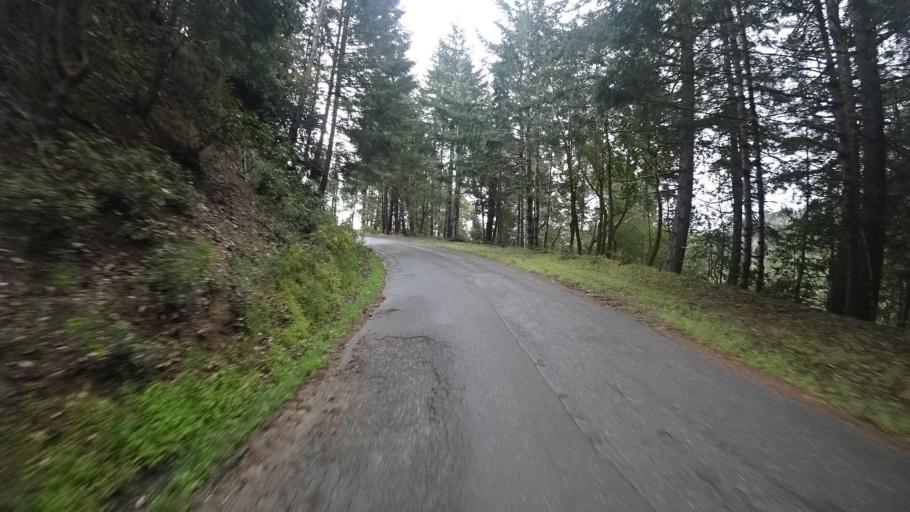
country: US
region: California
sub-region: Humboldt County
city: Redway
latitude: 40.2663
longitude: -123.7682
